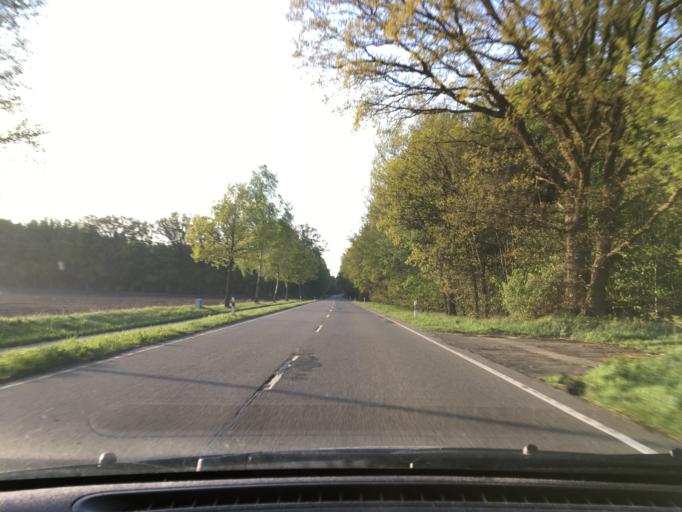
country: DE
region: Lower Saxony
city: Bispingen
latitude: 53.0318
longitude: 9.9996
